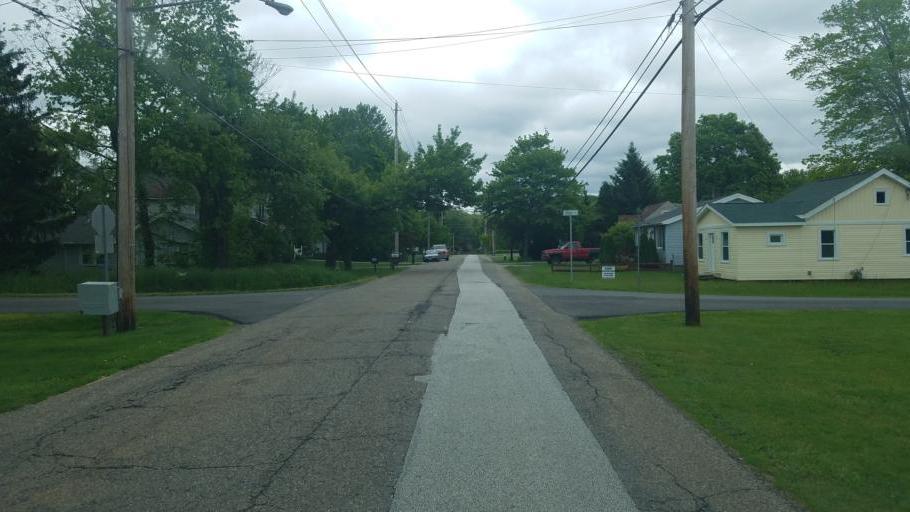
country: US
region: Ohio
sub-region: Summit County
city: Reminderville
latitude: 41.3457
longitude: -81.3802
